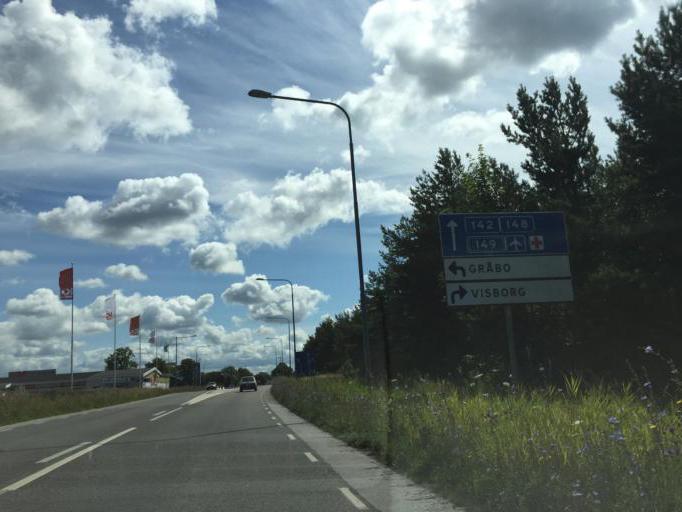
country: SE
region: Gotland
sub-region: Gotland
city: Visby
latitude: 57.6185
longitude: 18.2826
